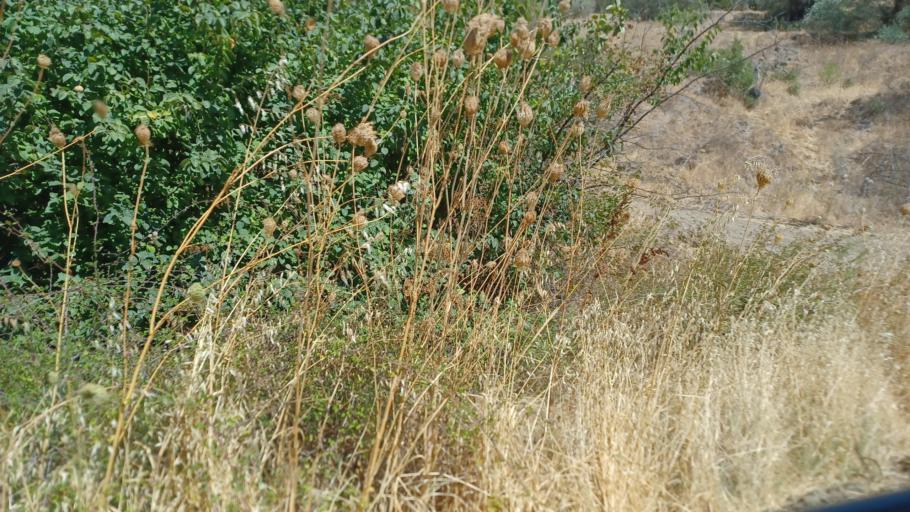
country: CY
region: Pafos
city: Mesogi
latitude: 34.9310
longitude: 32.6330
